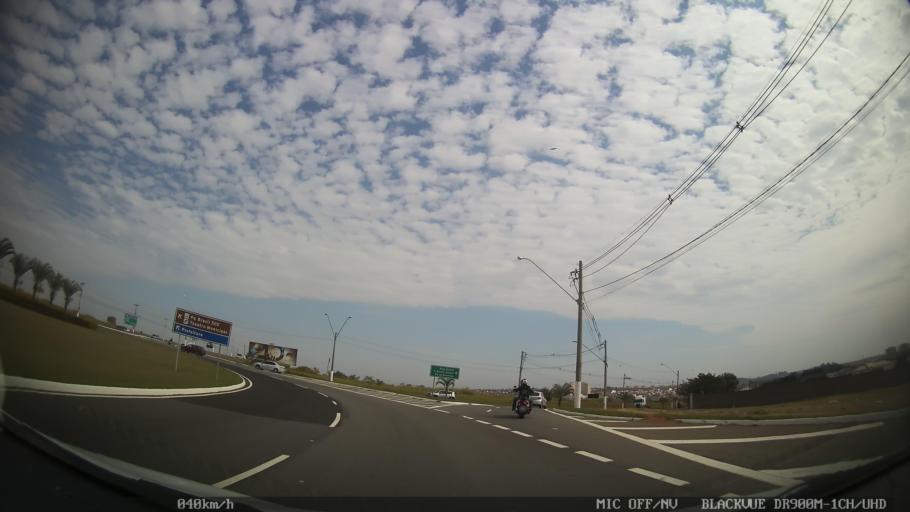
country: BR
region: Sao Paulo
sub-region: Paulinia
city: Paulinia
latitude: -22.7881
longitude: -47.1678
